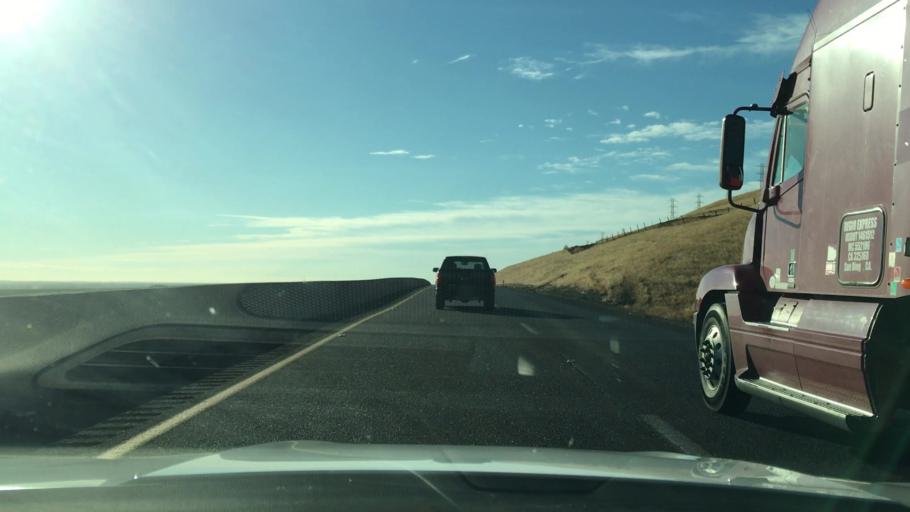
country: US
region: California
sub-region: Merced County
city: Los Banos
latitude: 36.9169
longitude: -120.8270
